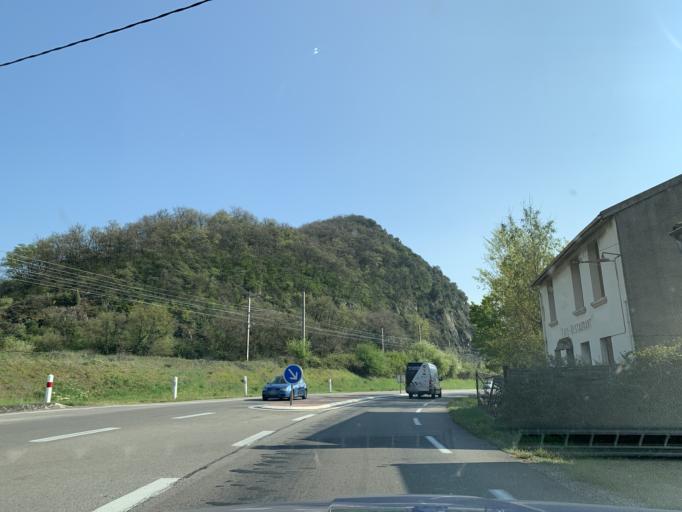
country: FR
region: Rhone-Alpes
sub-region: Departement de l'Ardeche
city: Saint-Jean-de-Muzols
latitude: 45.0948
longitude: 4.8357
